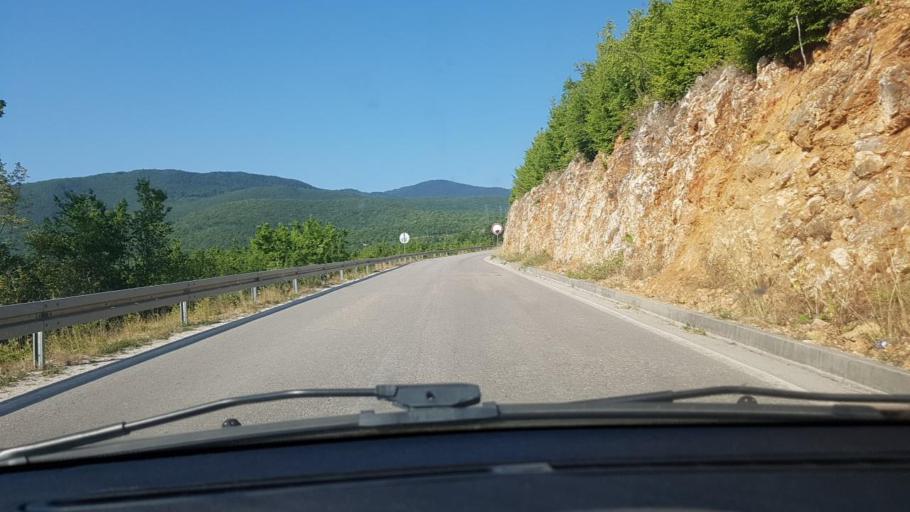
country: BA
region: Federation of Bosnia and Herzegovina
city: Rumboci
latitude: 43.8266
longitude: 17.4856
